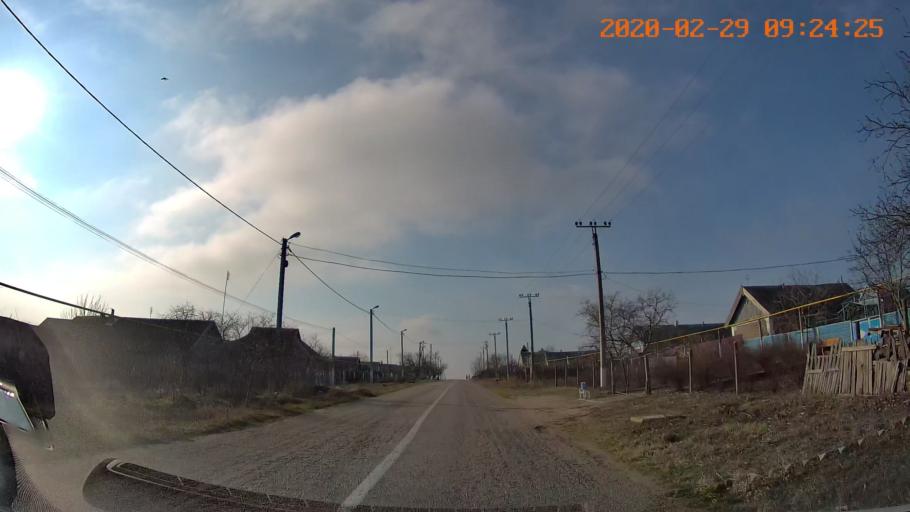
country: MD
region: Telenesti
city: Pervomaisc
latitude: 46.7164
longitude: 29.9587
